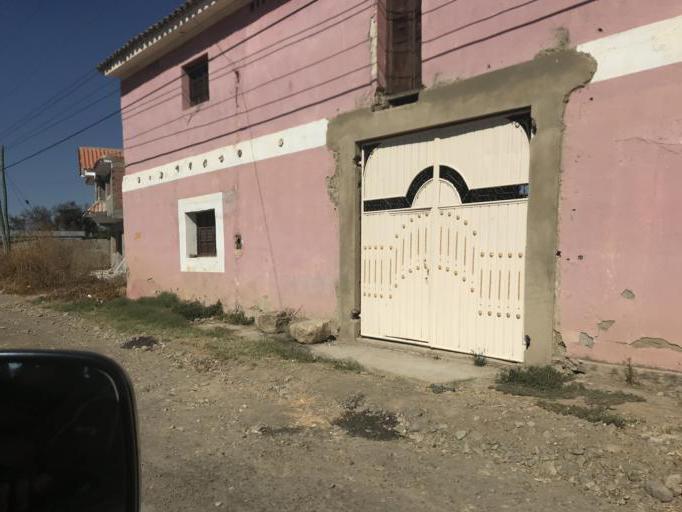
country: BO
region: Cochabamba
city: Punata
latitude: -17.5639
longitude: -65.8832
